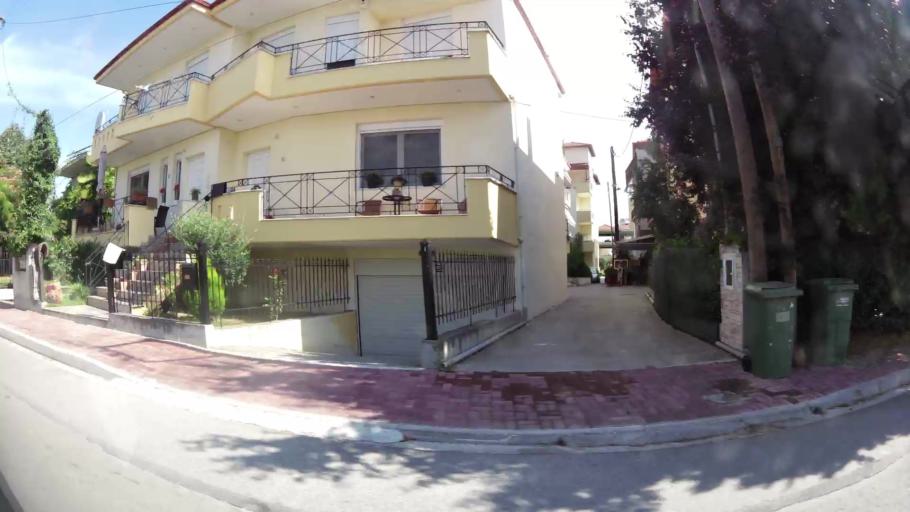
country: GR
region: Central Macedonia
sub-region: Nomos Pierias
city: Katerini
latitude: 40.2807
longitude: 22.4935
